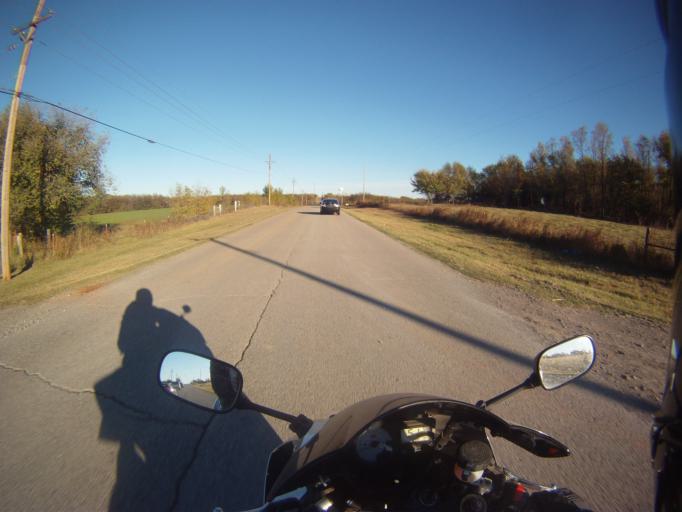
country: US
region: Oklahoma
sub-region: Payne County
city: Stillwater
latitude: 36.1303
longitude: -97.1100
